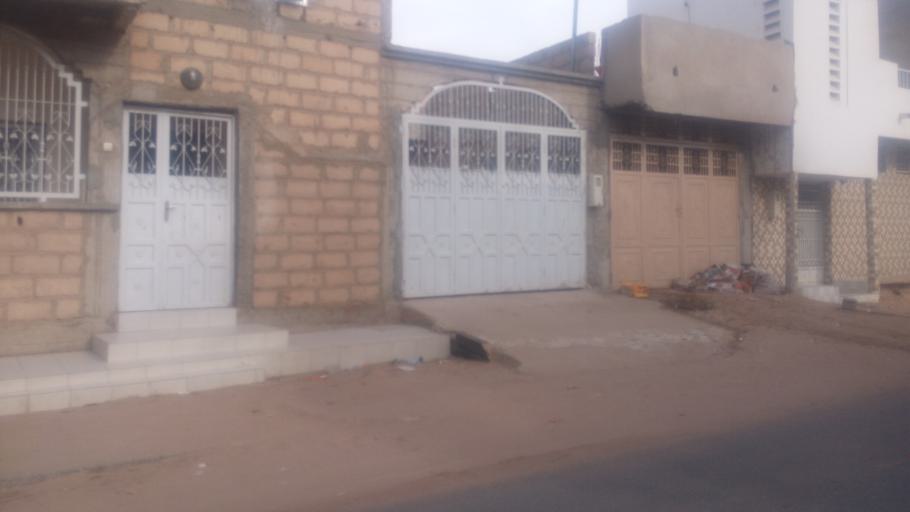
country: SN
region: Diourbel
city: Touba
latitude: 14.8649
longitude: -15.8738
